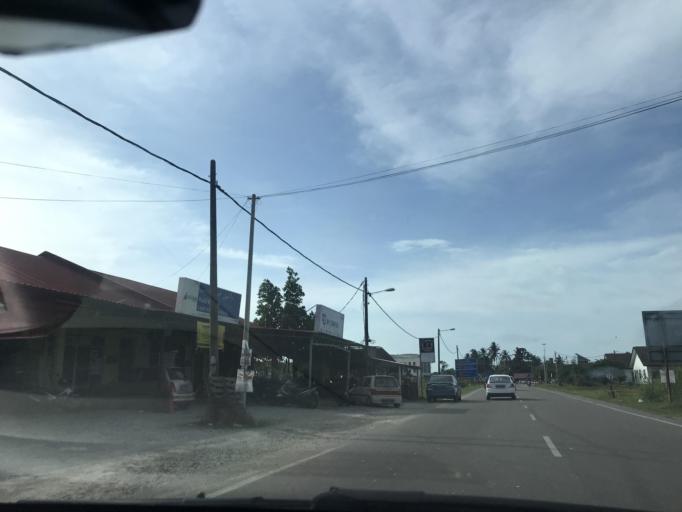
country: MY
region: Kelantan
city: Kota Bharu
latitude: 6.1377
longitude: 102.2025
